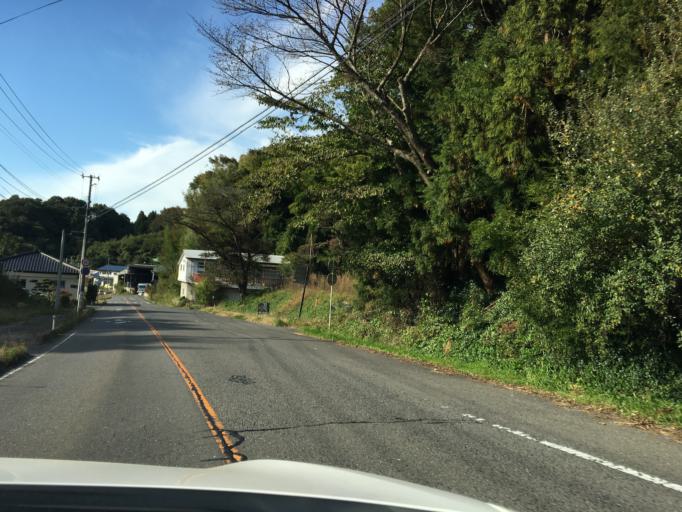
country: JP
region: Fukushima
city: Miharu
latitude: 37.3606
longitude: 140.5049
